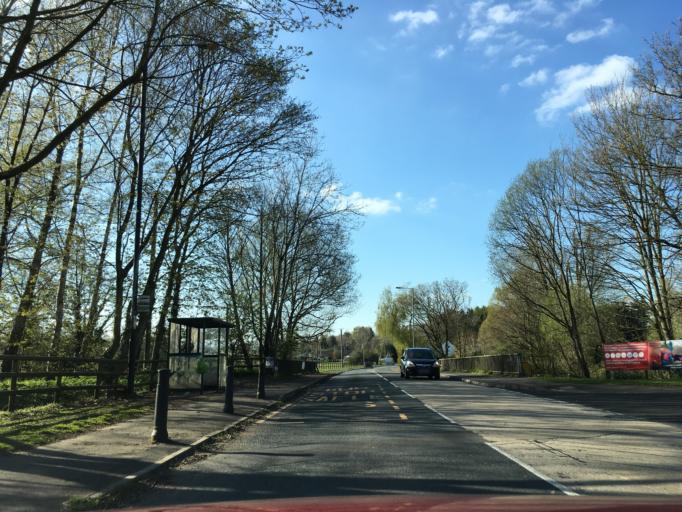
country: GB
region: Wales
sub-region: Monmouthshire
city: Usk
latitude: 51.7124
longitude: -2.9196
